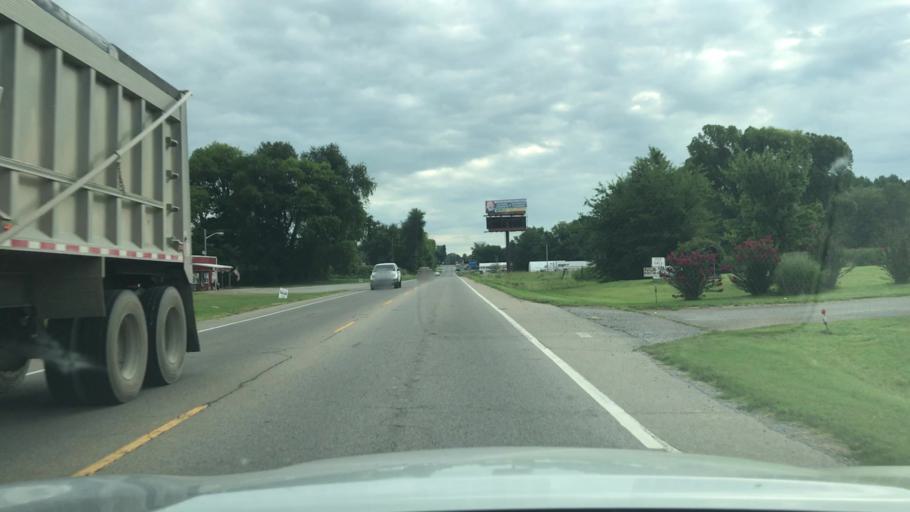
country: US
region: Kentucky
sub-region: Todd County
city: Guthrie
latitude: 36.6406
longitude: -87.2052
